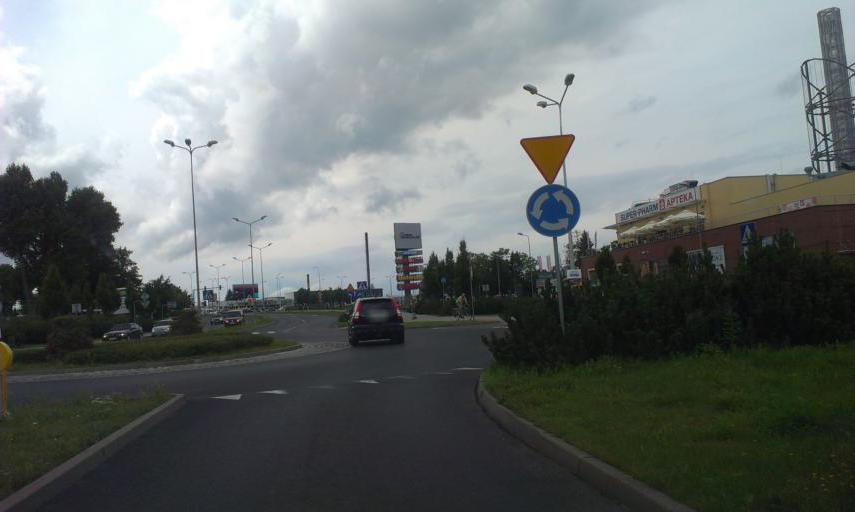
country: PL
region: West Pomeranian Voivodeship
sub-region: Koszalin
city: Koszalin
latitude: 54.1764
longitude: 16.2022
